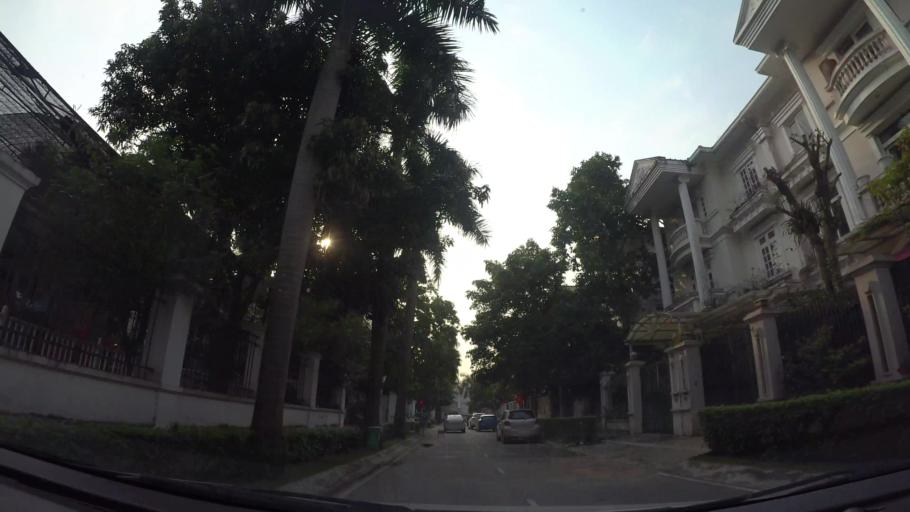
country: VN
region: Ha Noi
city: Tay Ho
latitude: 21.0756
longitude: 105.8021
